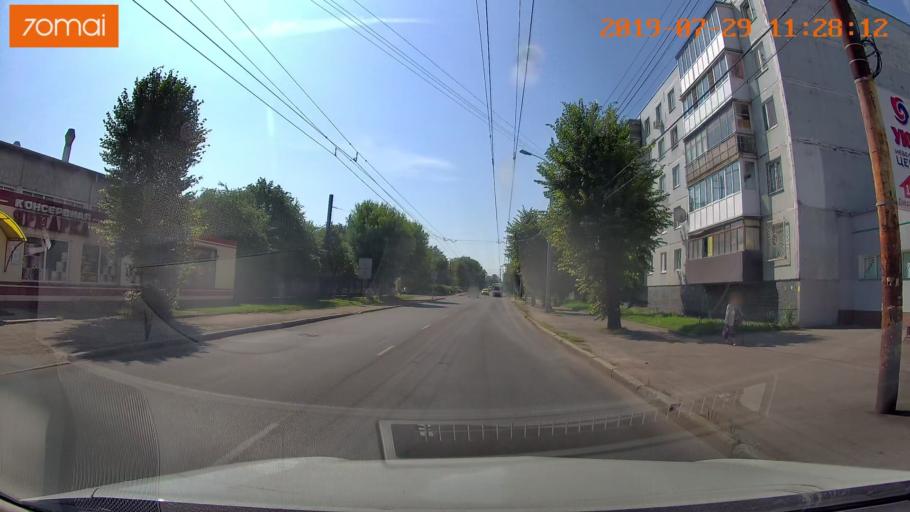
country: RU
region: Kaliningrad
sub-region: Gorod Kaliningrad
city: Kaliningrad
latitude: 54.6882
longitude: 20.5324
